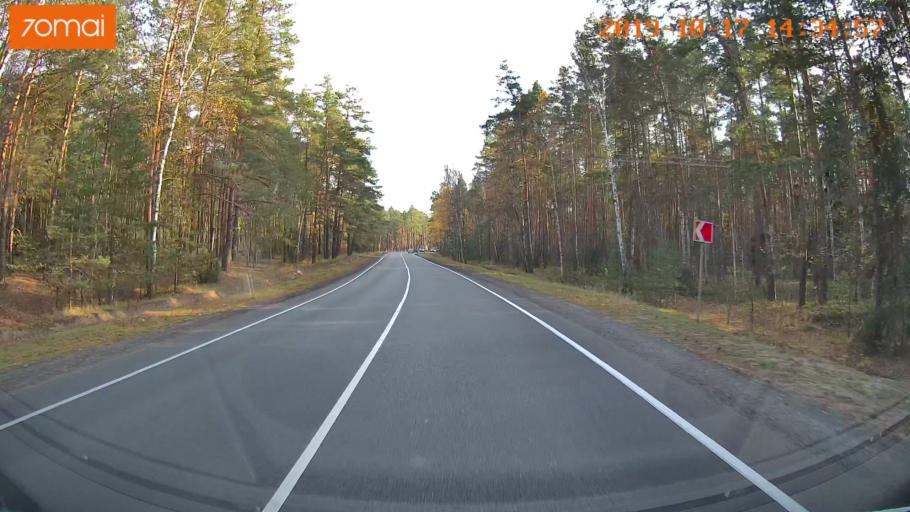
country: RU
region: Rjazan
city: Solotcha
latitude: 54.9053
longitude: 40.0007
